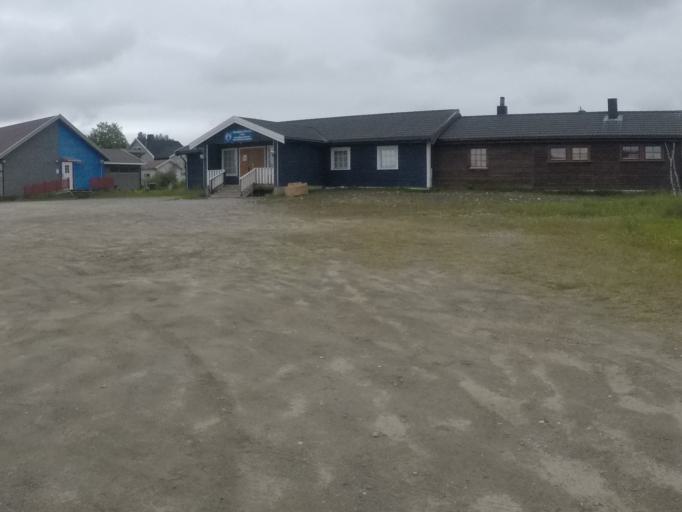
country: NO
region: Finnmark Fylke
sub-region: Kautokeino
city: Kautokeino
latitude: 69.0089
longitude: 23.0478
